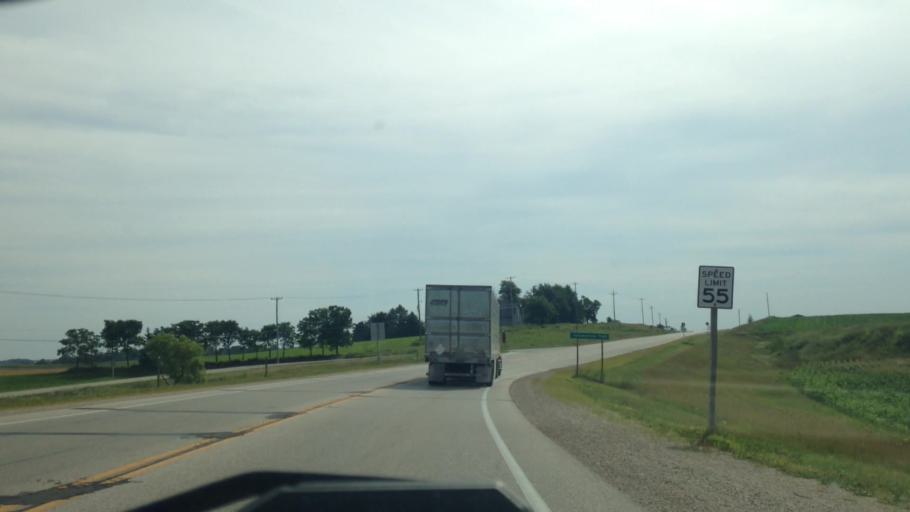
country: US
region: Wisconsin
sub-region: Washington County
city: Hartford
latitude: 43.4214
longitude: -88.3734
